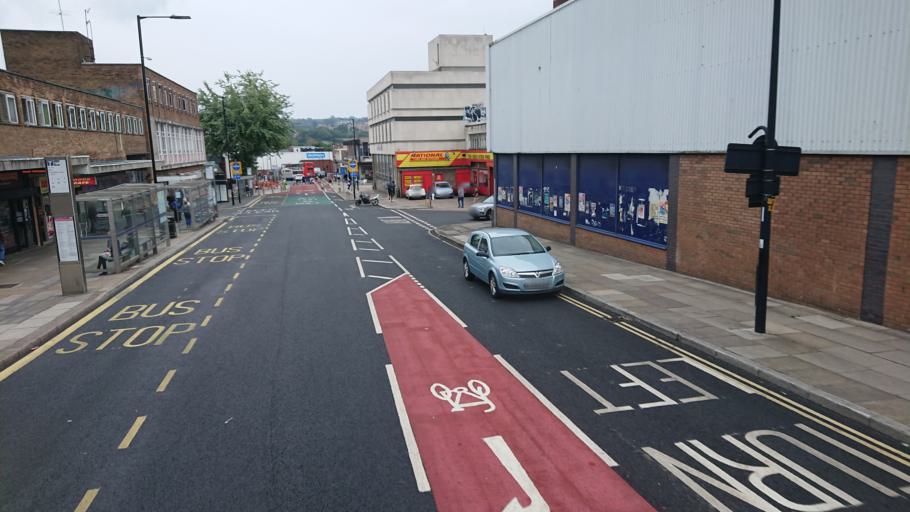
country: GB
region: England
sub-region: Sheffield
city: Sheffield
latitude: 53.3755
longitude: -1.4760
